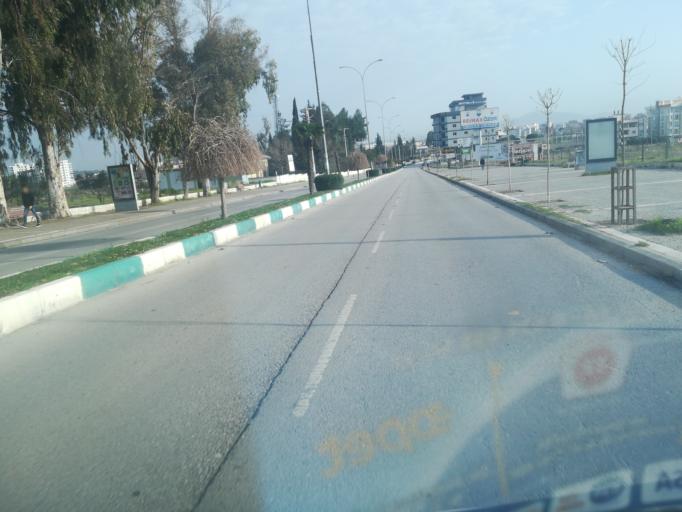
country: TR
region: Osmaniye
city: Osmaniye
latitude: 37.0469
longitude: 36.2268
